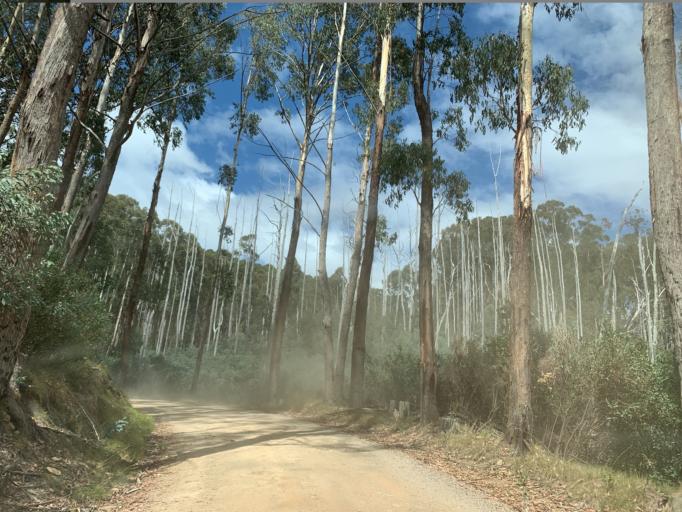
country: AU
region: Victoria
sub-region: Mansfield
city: Mansfield
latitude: -37.0977
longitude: 146.5334
